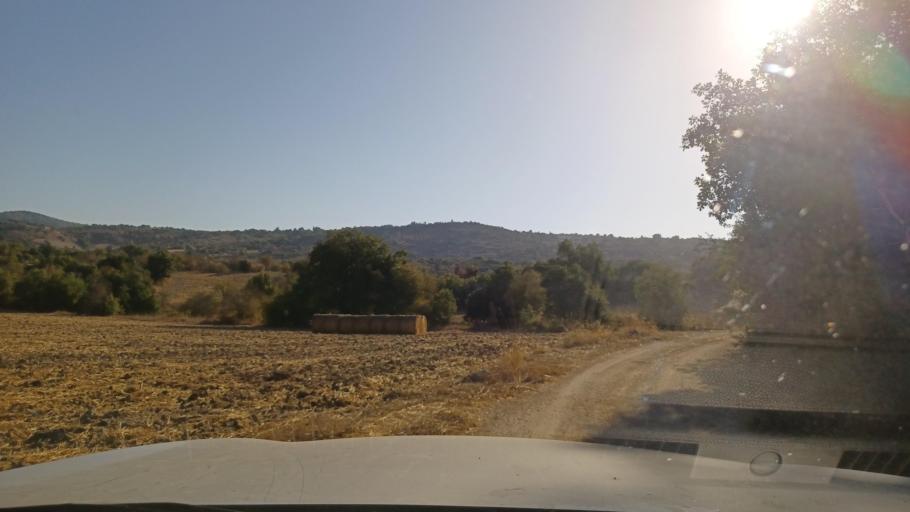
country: CY
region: Pafos
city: Polis
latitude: 34.9942
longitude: 32.4897
